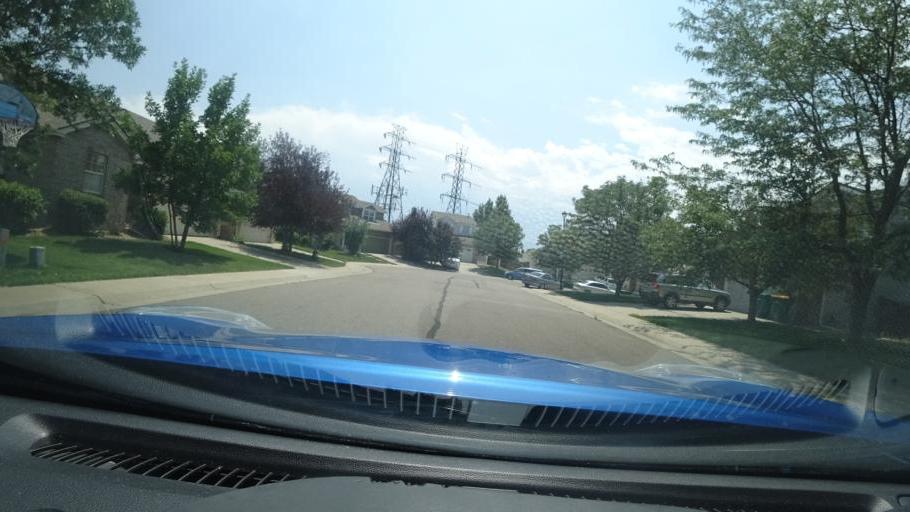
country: US
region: Colorado
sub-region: Adams County
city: Aurora
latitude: 39.6685
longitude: -104.7541
